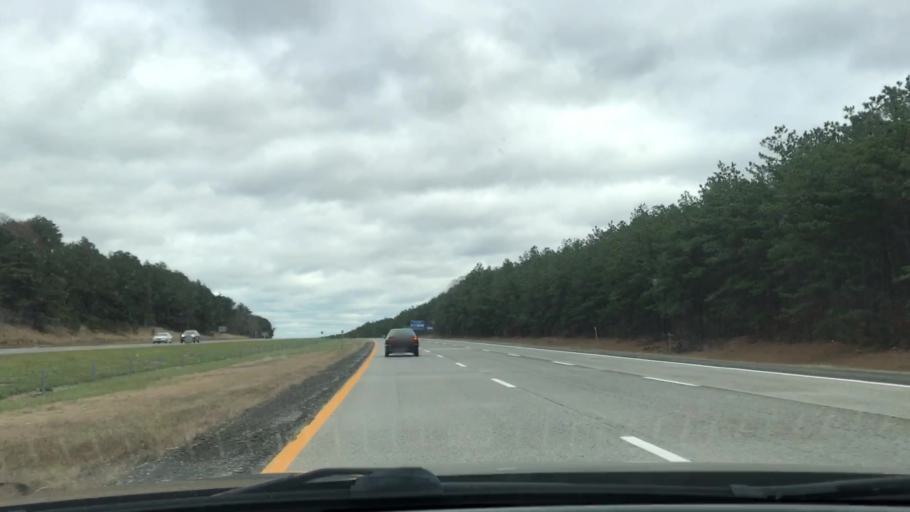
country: US
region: New York
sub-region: Suffolk County
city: Calverton
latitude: 40.8924
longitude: -72.7509
